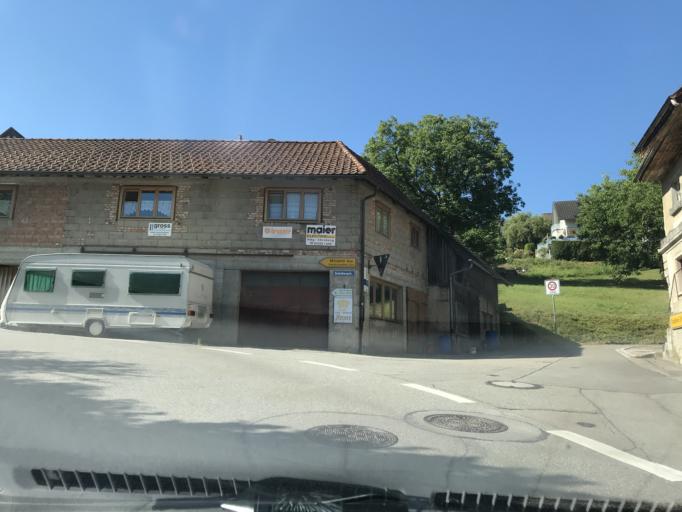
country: DE
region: Baden-Wuerttemberg
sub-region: Freiburg Region
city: Schopfheim
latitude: 47.6329
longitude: 7.8122
